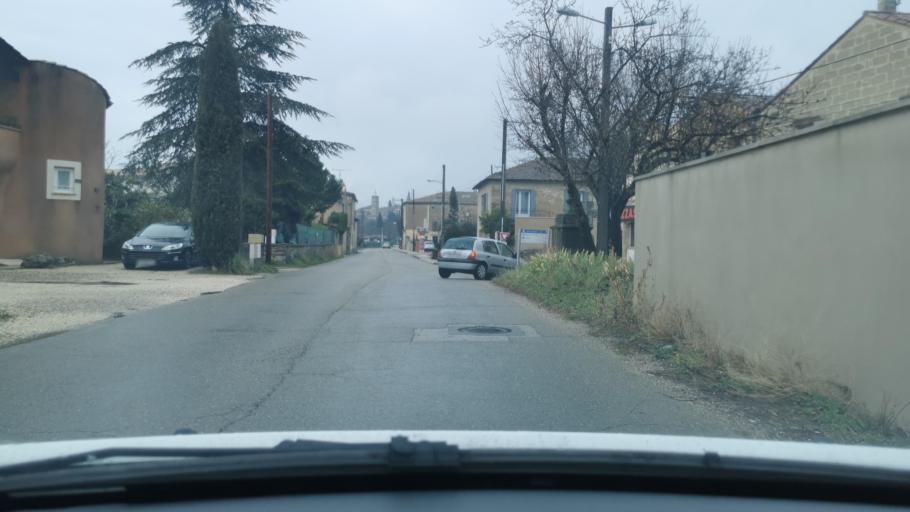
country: FR
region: Languedoc-Roussillon
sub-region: Departement du Gard
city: Saint-Quentin-la-Poterie
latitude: 44.0398
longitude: 4.4435
